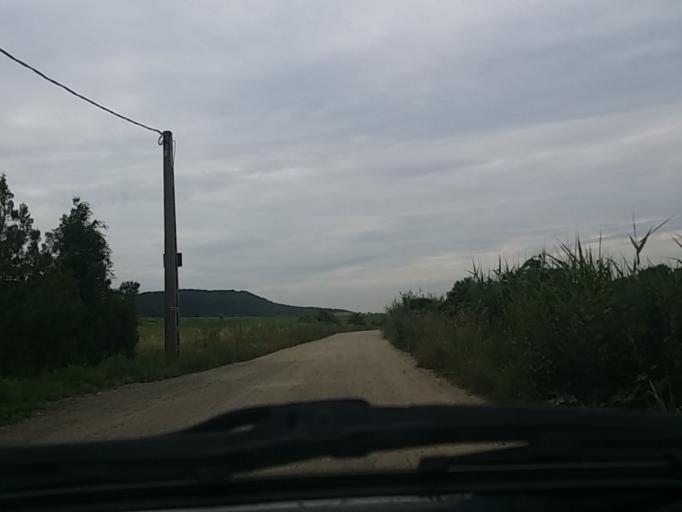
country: HU
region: Pest
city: Pilisborosjeno
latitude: 47.6050
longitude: 18.9640
